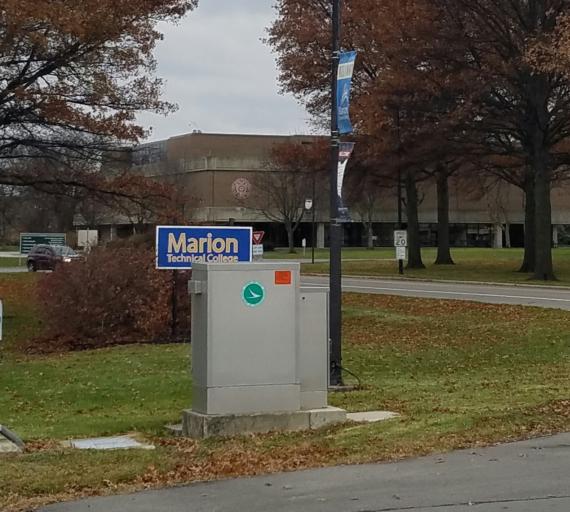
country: US
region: Ohio
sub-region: Marion County
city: Marion
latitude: 40.5811
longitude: -83.0898
